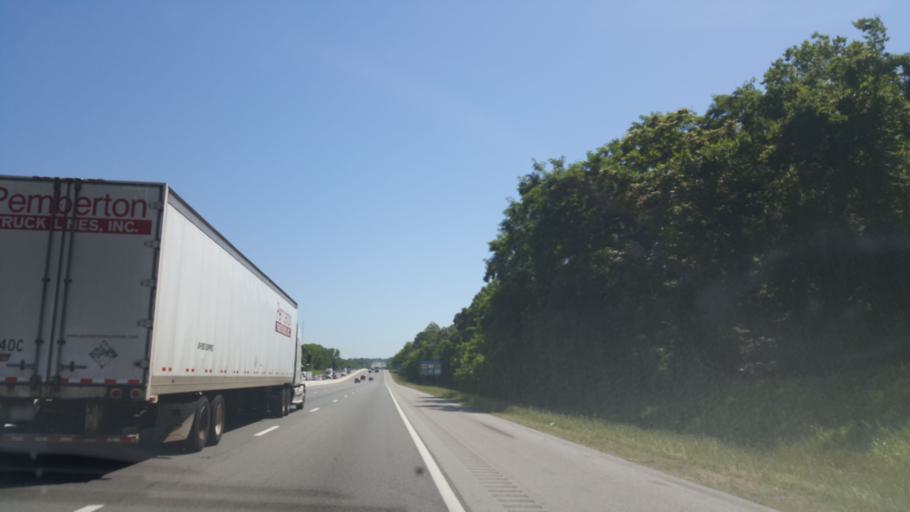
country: US
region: Tennessee
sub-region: Davidson County
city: Lakewood
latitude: 36.1487
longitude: -86.6404
